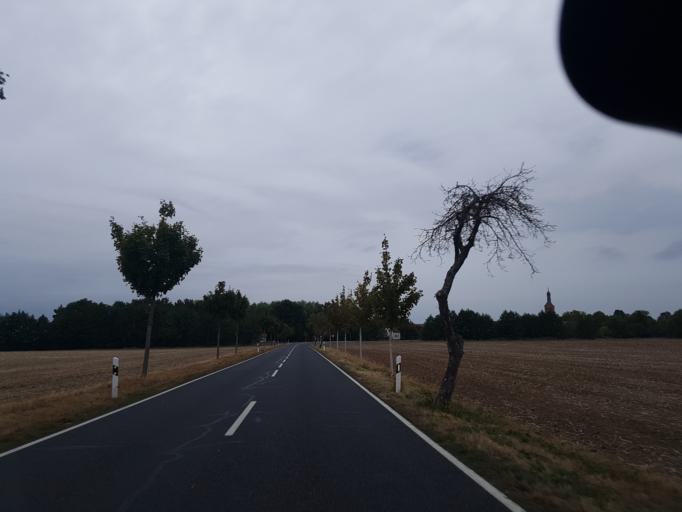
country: DE
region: Saxony-Anhalt
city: Prettin
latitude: 51.6961
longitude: 12.8889
